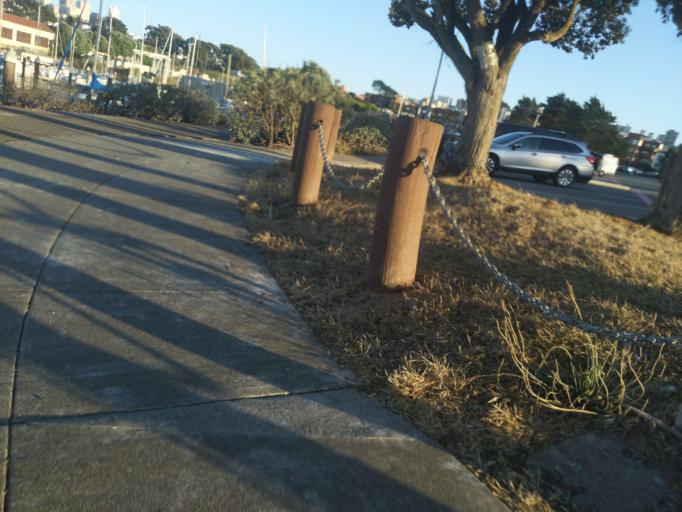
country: US
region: California
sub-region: San Francisco County
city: San Francisco
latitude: 37.8069
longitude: -122.4343
